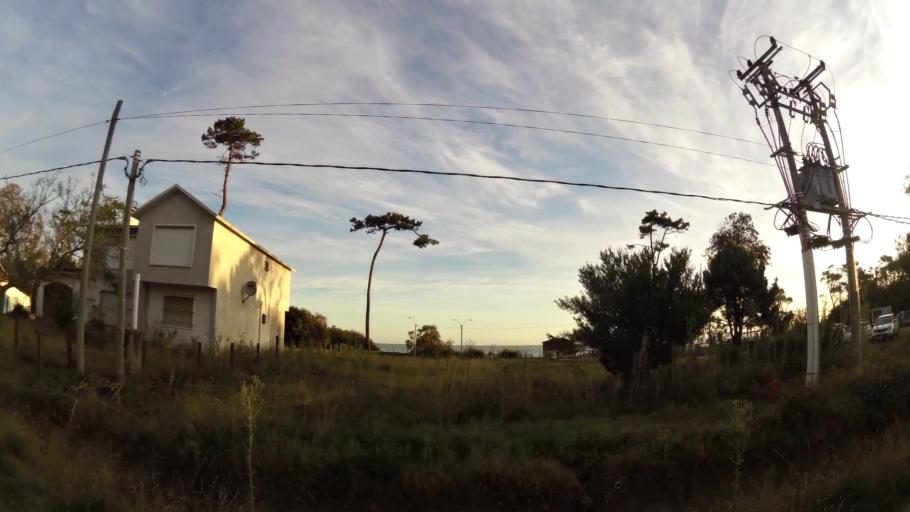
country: UY
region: Canelones
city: Atlantida
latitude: -34.7699
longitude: -55.7788
